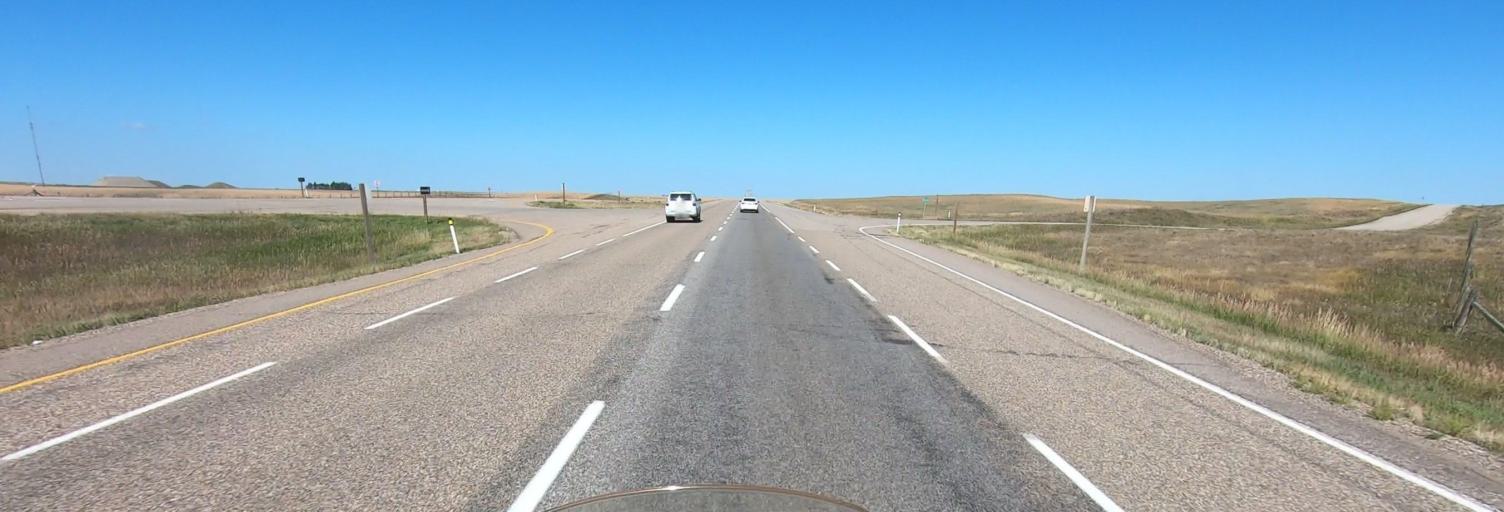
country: CA
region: Alberta
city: Bassano
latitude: 50.8563
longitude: -112.8436
